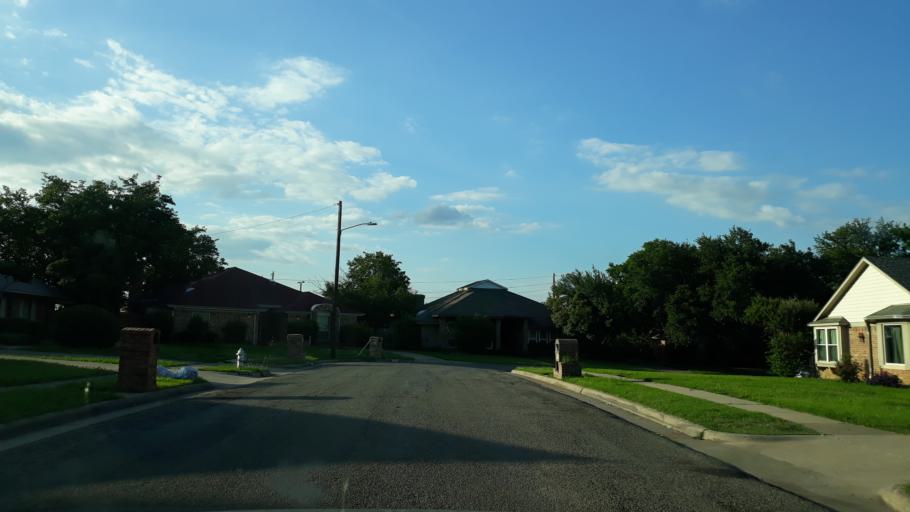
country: US
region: Texas
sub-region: Dallas County
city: Irving
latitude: 32.8633
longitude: -97.0000
